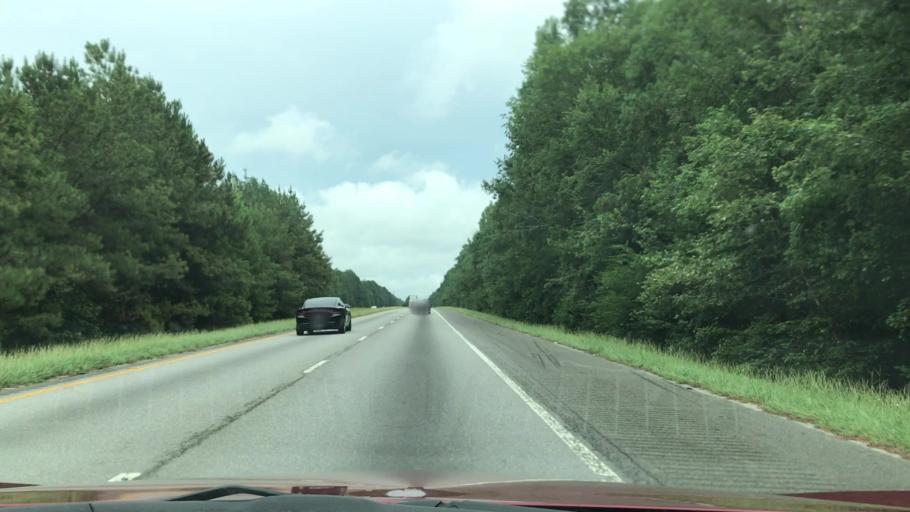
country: US
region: South Carolina
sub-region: Orangeburg County
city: Brookdale
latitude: 33.4447
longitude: -80.7131
